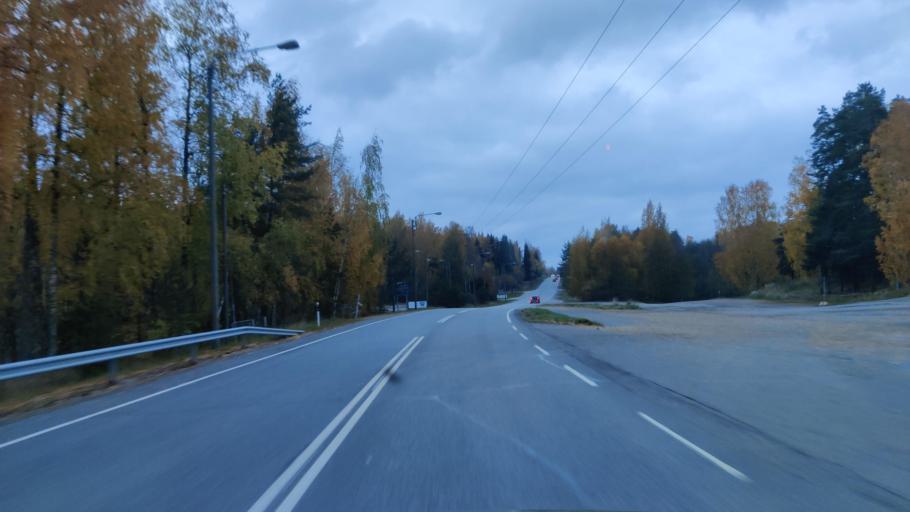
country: FI
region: Uusimaa
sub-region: Helsinki
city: Lohja
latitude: 60.3625
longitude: 24.1683
